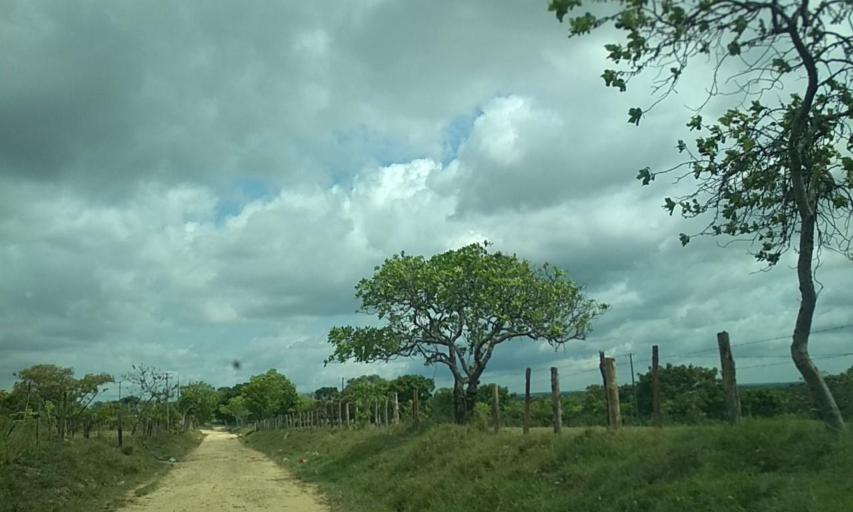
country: MX
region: Veracruz
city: Las Choapas
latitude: 17.8918
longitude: -94.1156
